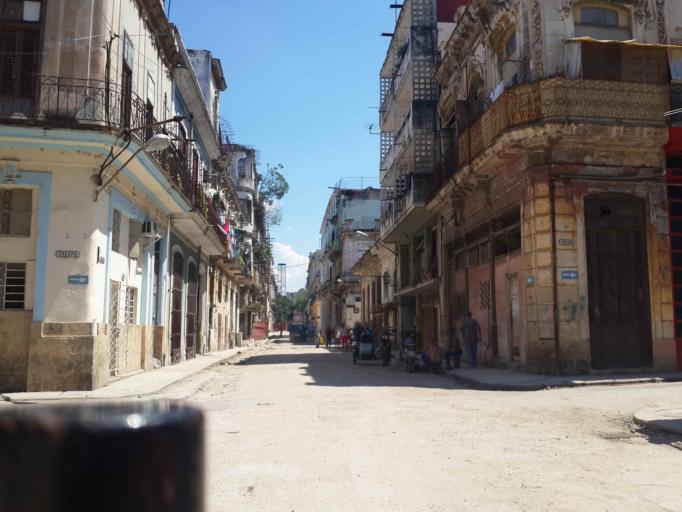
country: CU
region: La Habana
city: Centro Habana
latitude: 23.1399
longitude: -82.3613
